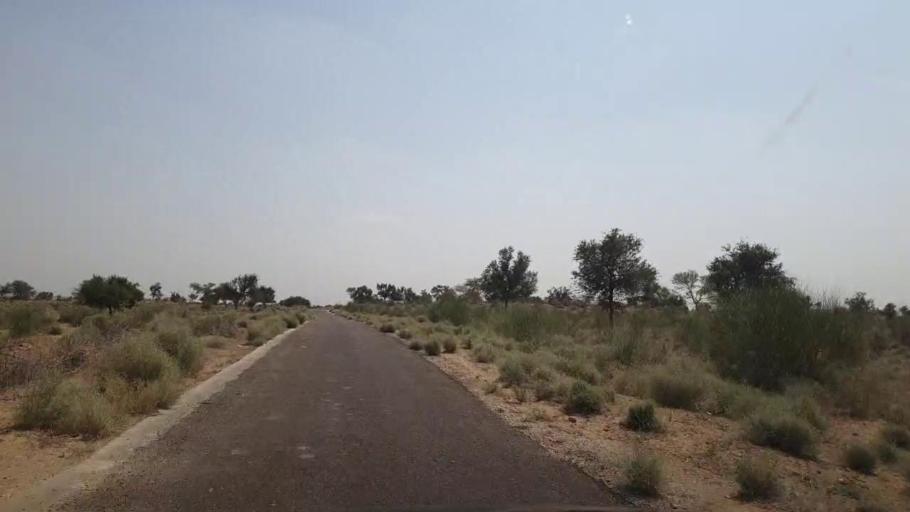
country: PK
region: Sindh
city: Islamkot
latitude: 25.0967
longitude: 70.7286
